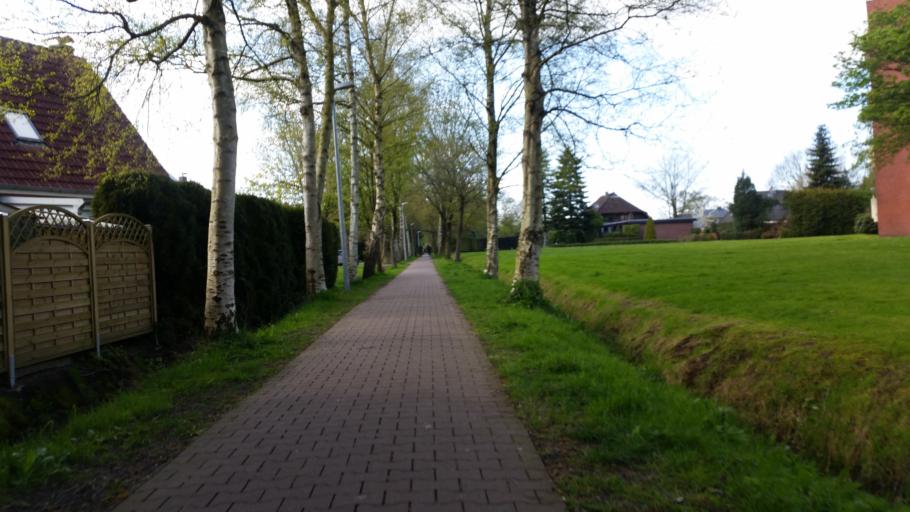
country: DE
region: Lower Saxony
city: Aurich
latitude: 53.4623
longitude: 7.4974
